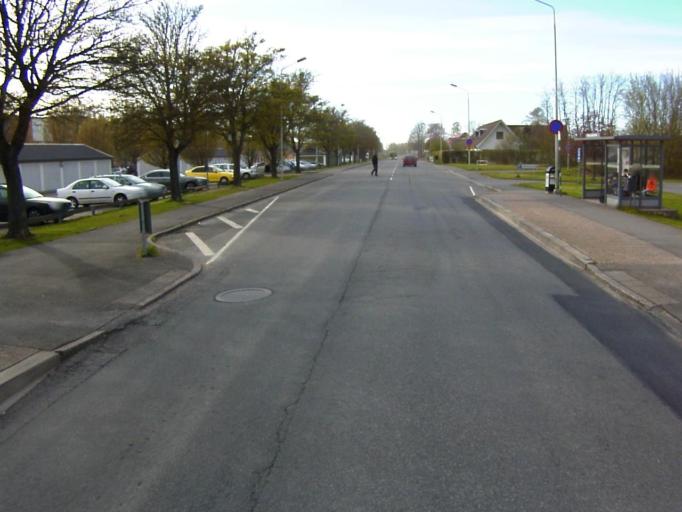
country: SE
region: Skane
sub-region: Kristianstads Kommun
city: Kristianstad
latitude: 56.0600
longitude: 14.1626
